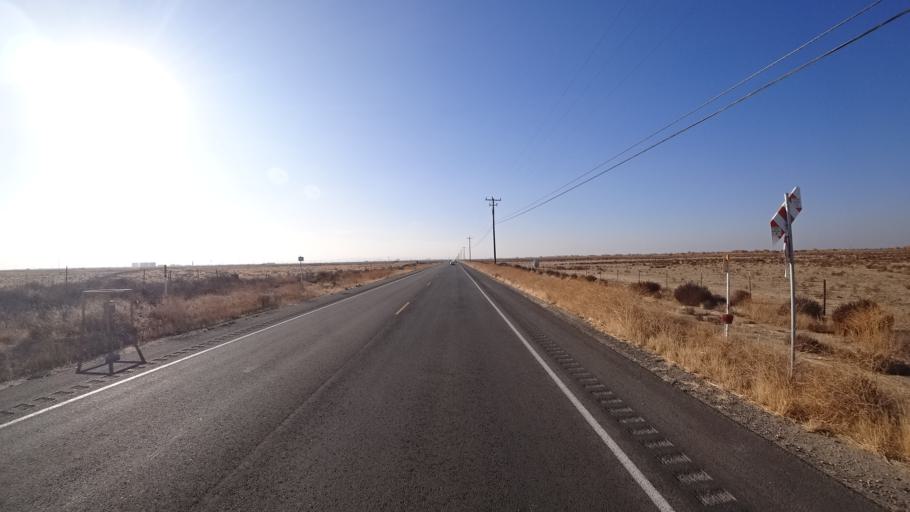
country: US
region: California
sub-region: Kern County
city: Rosedale
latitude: 35.2961
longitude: -119.2015
